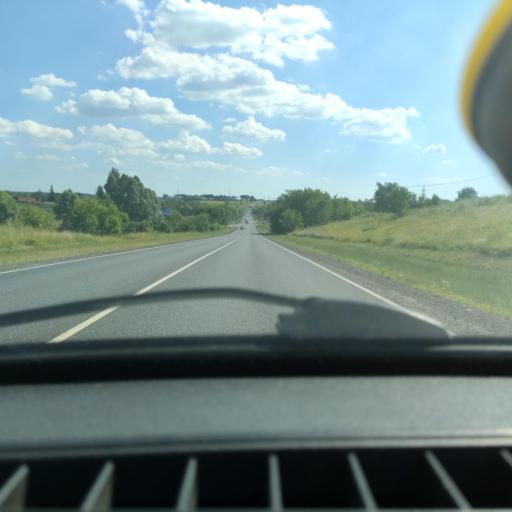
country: RU
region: Samara
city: Povolzhskiy
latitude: 53.7130
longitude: 49.7475
